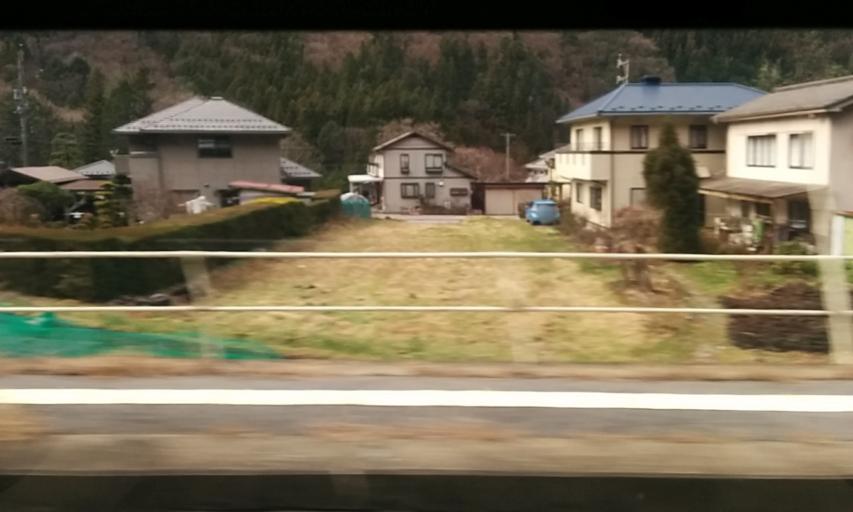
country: JP
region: Nagano
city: Shiojiri
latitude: 36.0487
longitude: 137.8945
